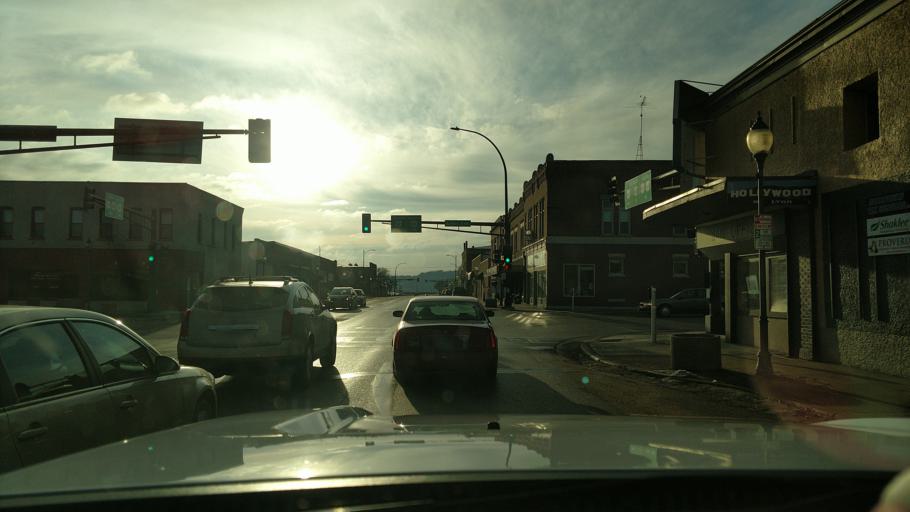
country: US
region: Minnesota
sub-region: Wabasha County
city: Lake City
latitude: 44.4496
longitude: -92.2671
